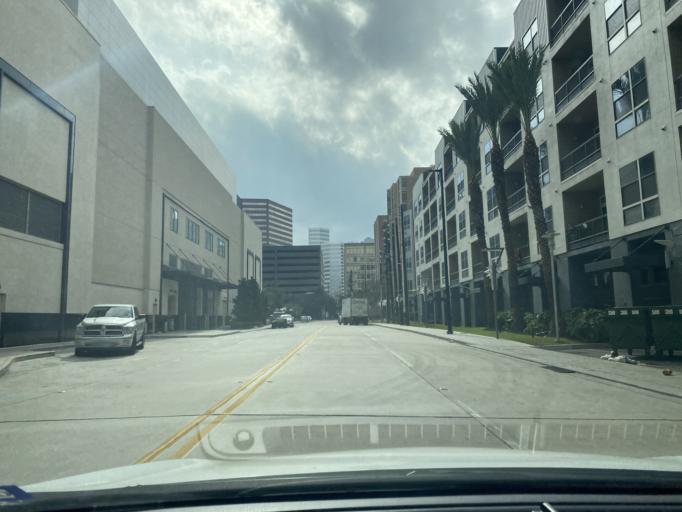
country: US
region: Texas
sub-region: Harris County
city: West University Place
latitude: 29.7521
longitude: -95.4578
